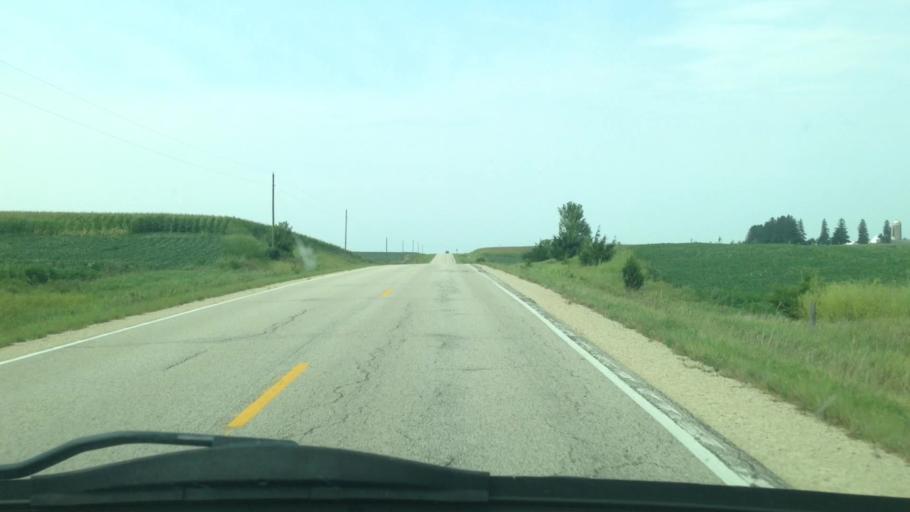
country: US
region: Minnesota
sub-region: Winona County
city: Saint Charles
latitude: 43.8554
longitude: -91.9593
